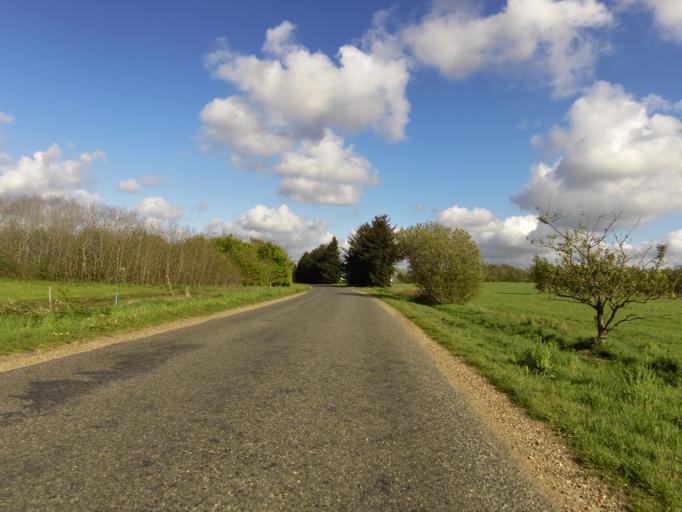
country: DK
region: South Denmark
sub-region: Esbjerg Kommune
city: Ribe
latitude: 55.2622
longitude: 8.7613
